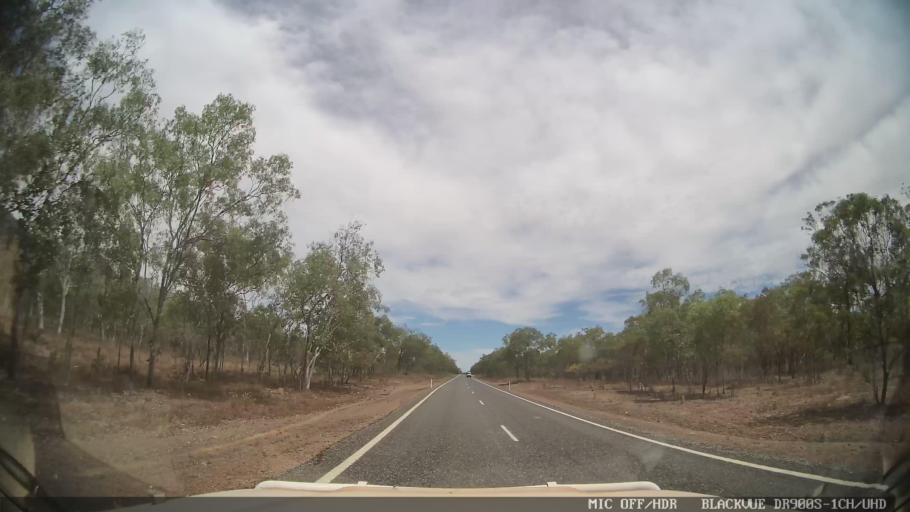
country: AU
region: Queensland
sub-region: Cairns
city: Port Douglas
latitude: -16.2437
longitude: 144.7269
